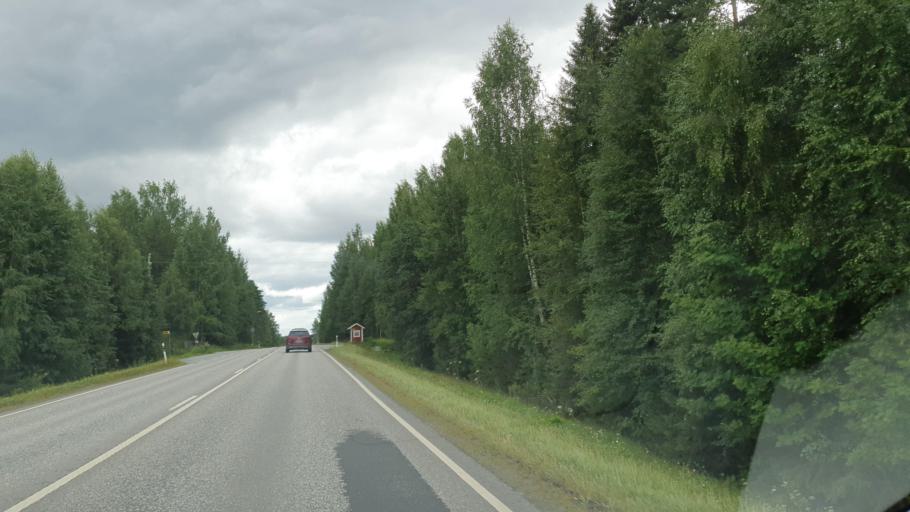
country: FI
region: Northern Savo
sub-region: Ylae-Savo
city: Sonkajaervi
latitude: 63.7408
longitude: 27.3811
